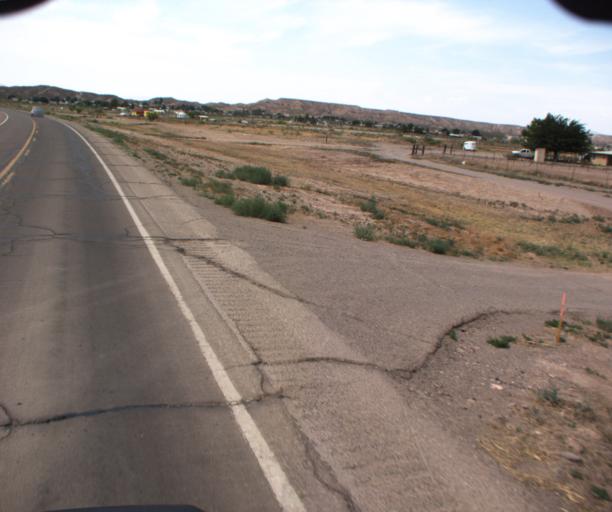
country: US
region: Arizona
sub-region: Greenlee County
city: Clifton
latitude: 32.7394
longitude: -109.0947
